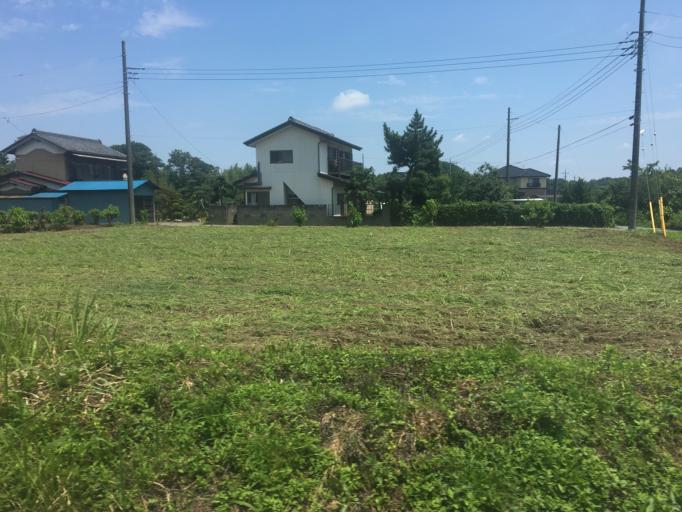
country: JP
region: Saitama
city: Yorii
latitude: 36.1111
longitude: 139.1841
